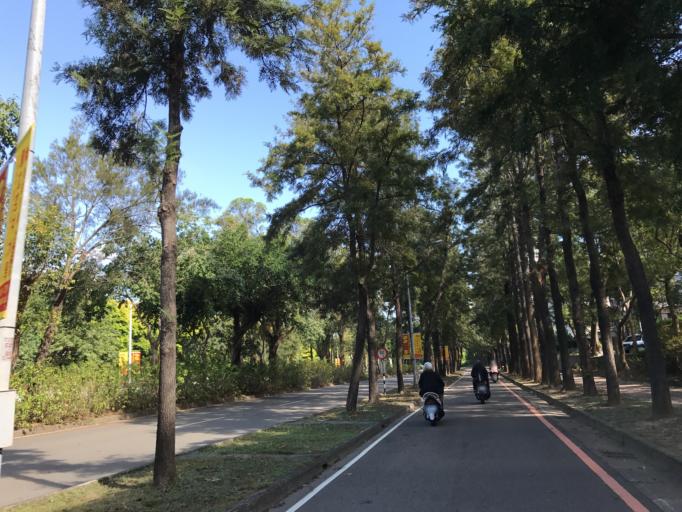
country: TW
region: Taiwan
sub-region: Hsinchu
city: Hsinchu
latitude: 24.7766
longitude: 121.0175
